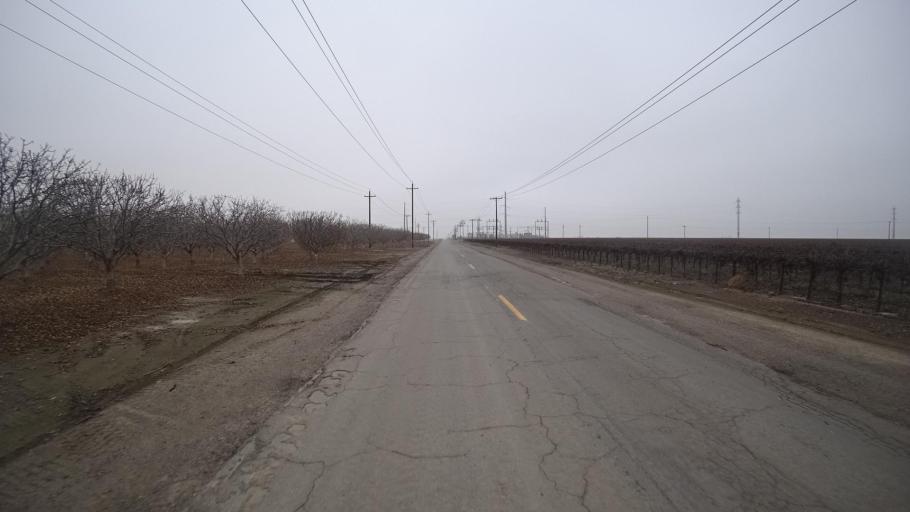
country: US
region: California
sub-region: Kern County
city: Wasco
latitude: 35.7175
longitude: -119.4522
